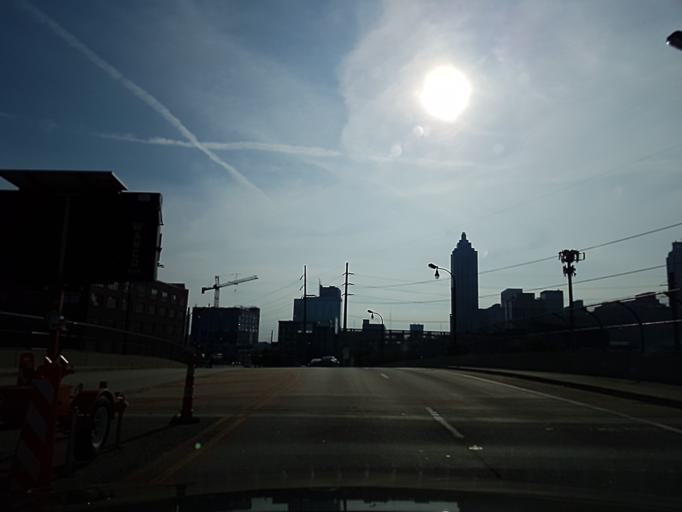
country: US
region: Georgia
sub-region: Fulton County
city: Atlanta
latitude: 33.7639
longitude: -84.3987
